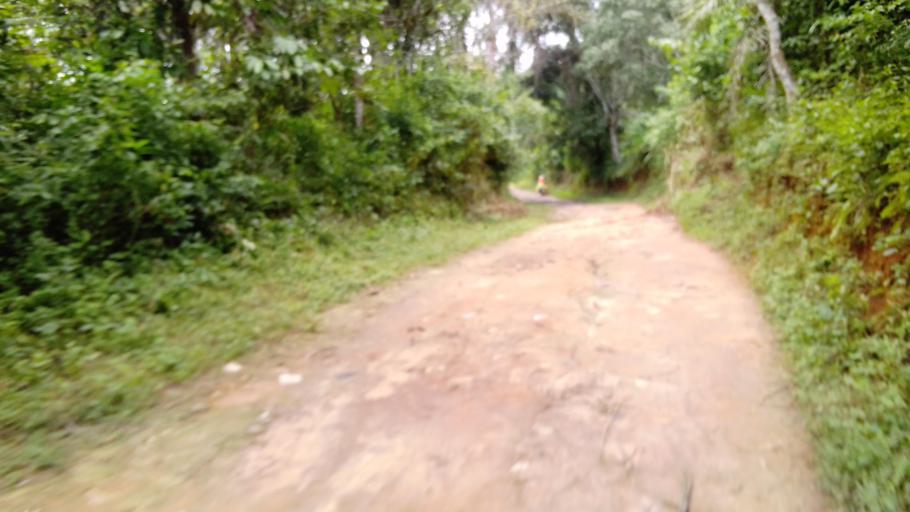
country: SL
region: Eastern Province
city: Koidu
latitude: 8.6592
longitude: -10.9354
